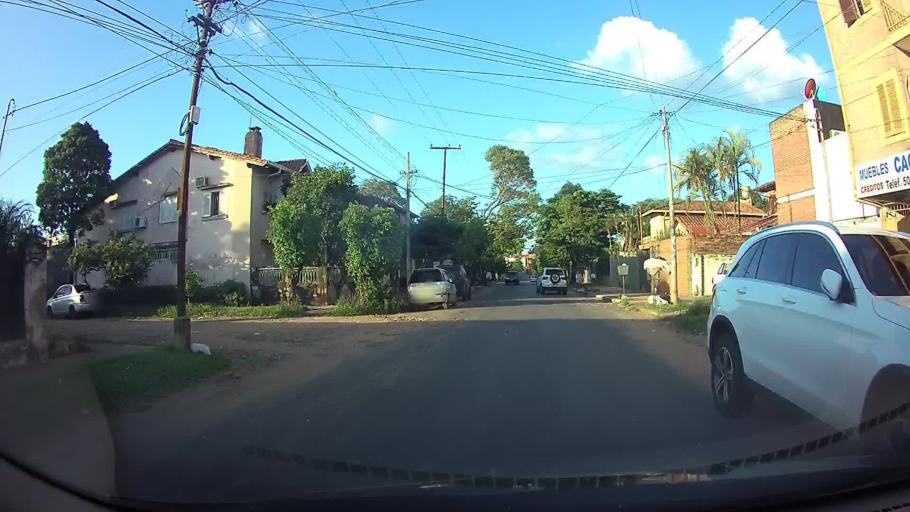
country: PY
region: Central
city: Lambare
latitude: -25.3198
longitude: -57.5710
